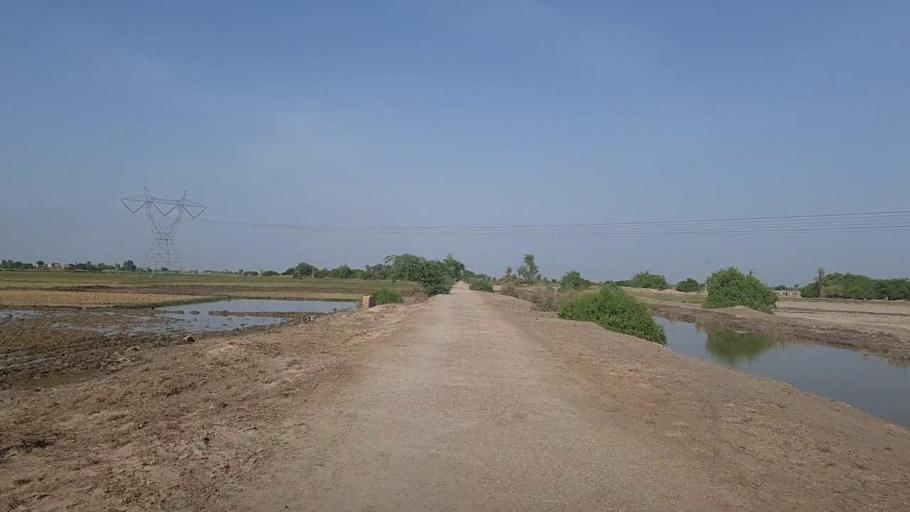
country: PK
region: Sindh
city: Sita Road
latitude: 27.0917
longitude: 67.8574
